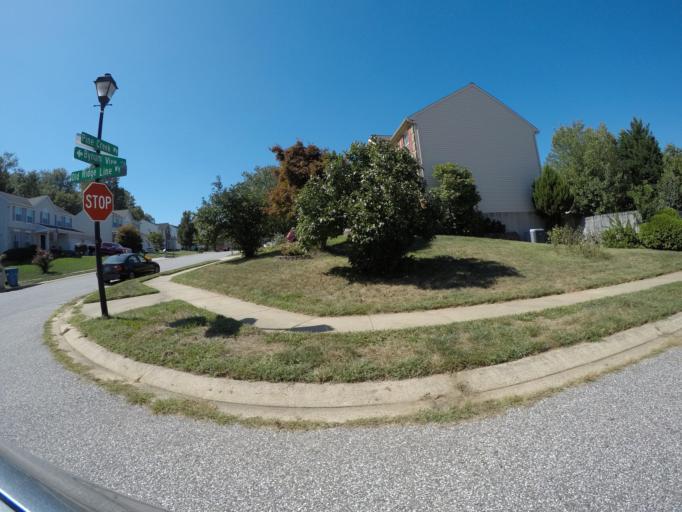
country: US
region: Maryland
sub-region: Harford County
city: Riverside
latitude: 39.4805
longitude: -76.2839
